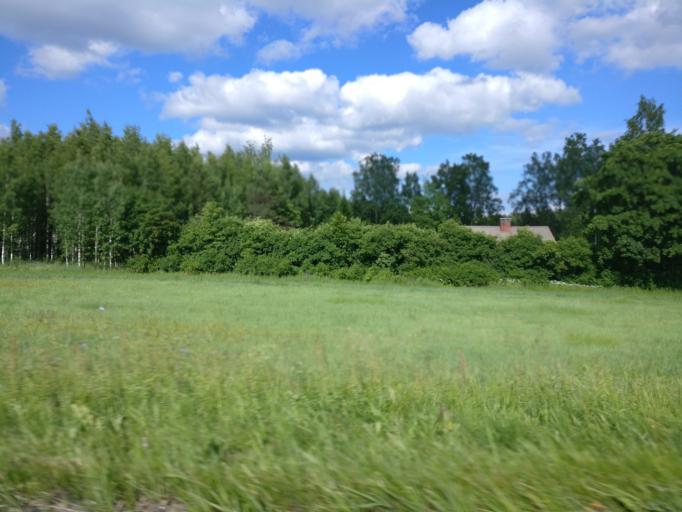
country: FI
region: Southern Savonia
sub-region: Savonlinna
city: Kerimaeki
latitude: 61.8688
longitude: 29.1300
